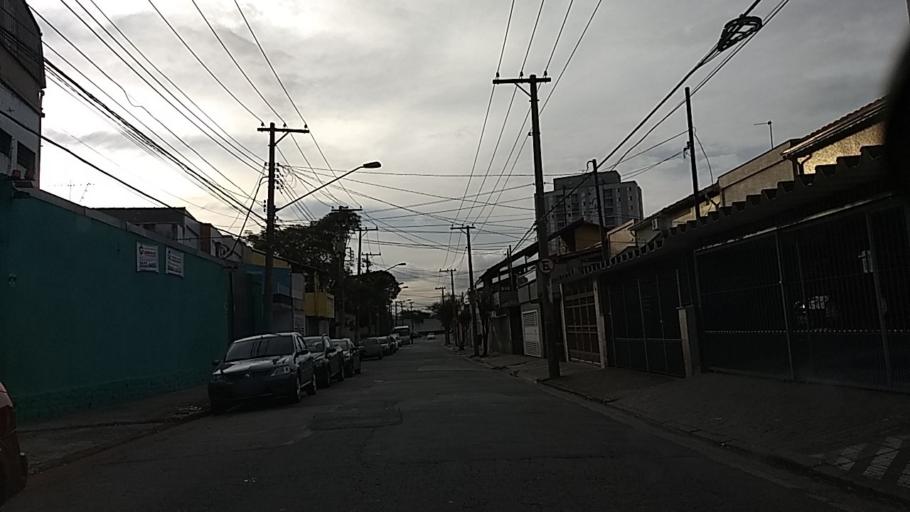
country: BR
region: Sao Paulo
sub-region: Sao Paulo
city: Sao Paulo
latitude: -23.5271
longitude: -46.6026
